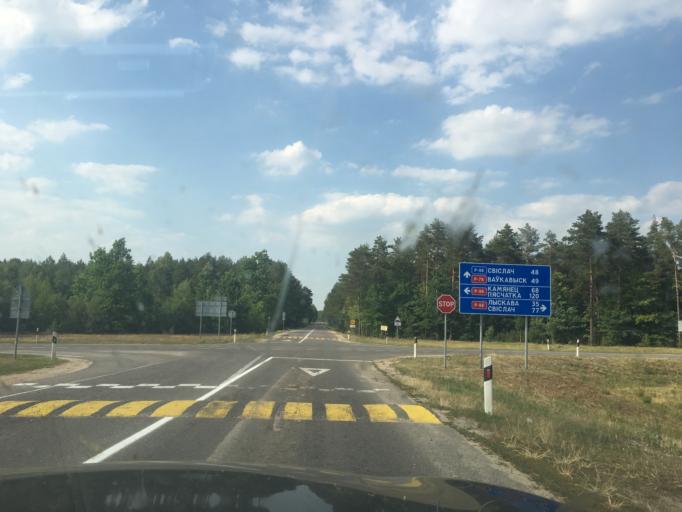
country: BY
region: Brest
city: Pruzhany
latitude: 52.7019
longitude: 24.3082
